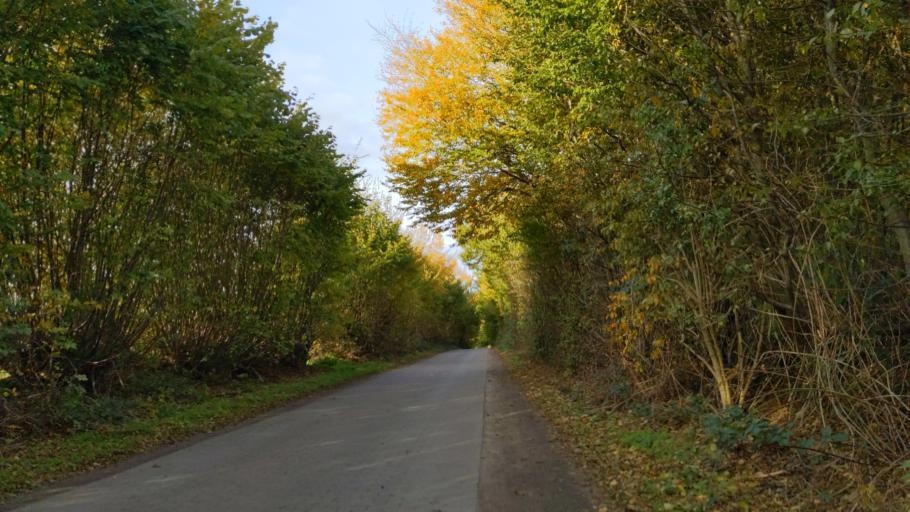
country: DE
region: Schleswig-Holstein
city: Eutin
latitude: 54.1495
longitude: 10.6293
